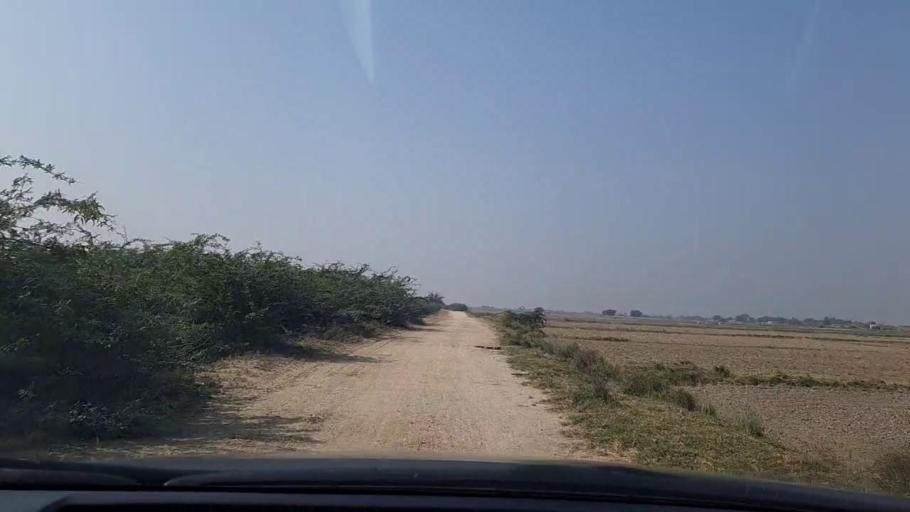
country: PK
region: Sindh
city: Mirpur Sakro
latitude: 24.5749
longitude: 67.7843
